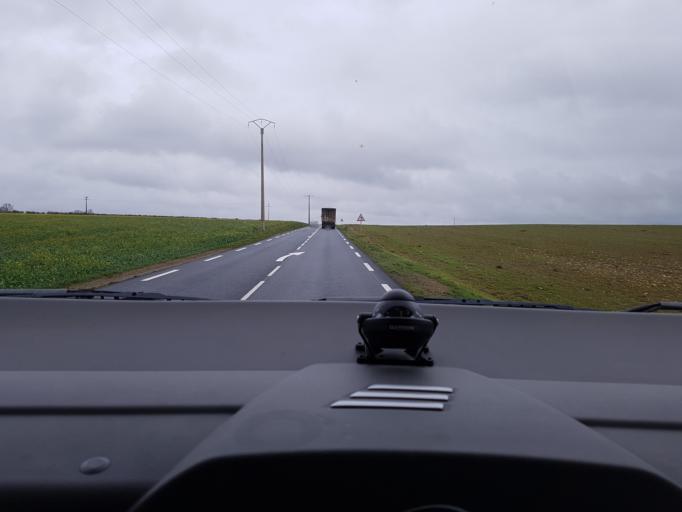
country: FR
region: Picardie
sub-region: Departement de l'Oise
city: Saint-Germer-de-Fly
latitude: 49.5057
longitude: 1.7970
